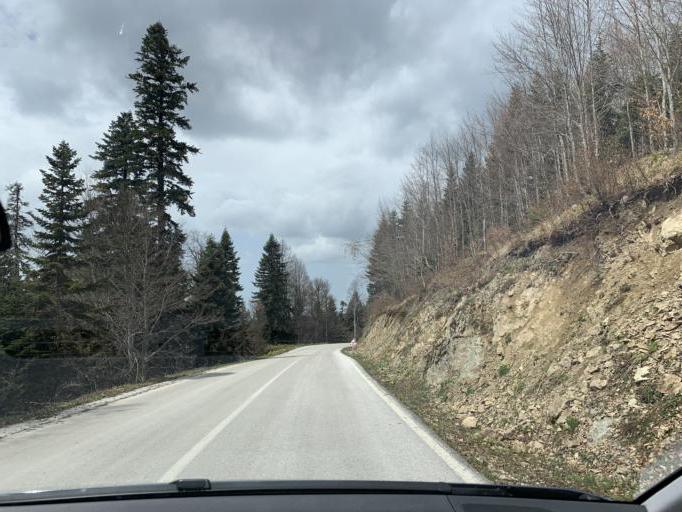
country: TR
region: Bolu
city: Bolu
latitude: 40.8928
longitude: 31.6732
